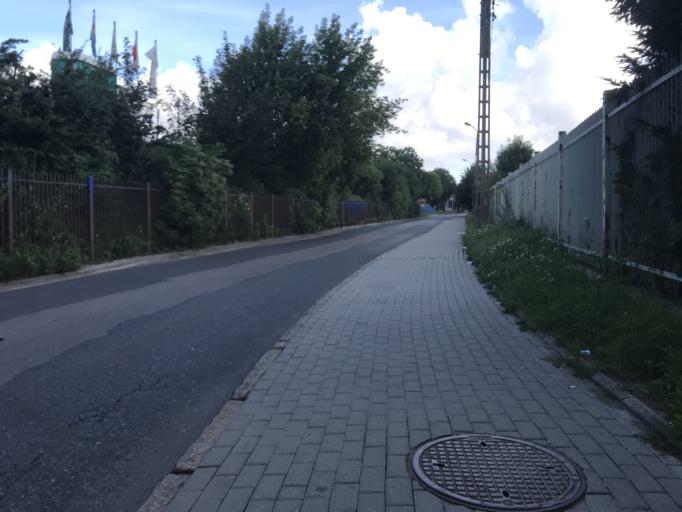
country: PL
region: Pomeranian Voivodeship
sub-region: Gdansk
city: Gdansk
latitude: 54.3461
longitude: 18.6727
